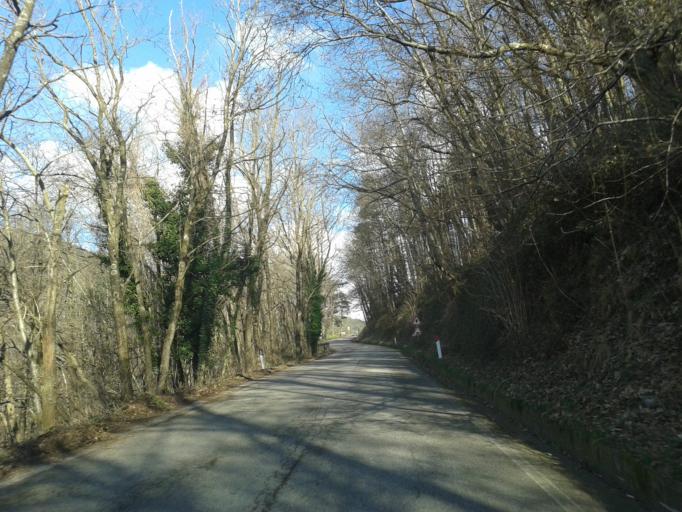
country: IT
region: Tuscany
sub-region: Province of Pisa
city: Calci
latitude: 43.7359
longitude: 10.5472
